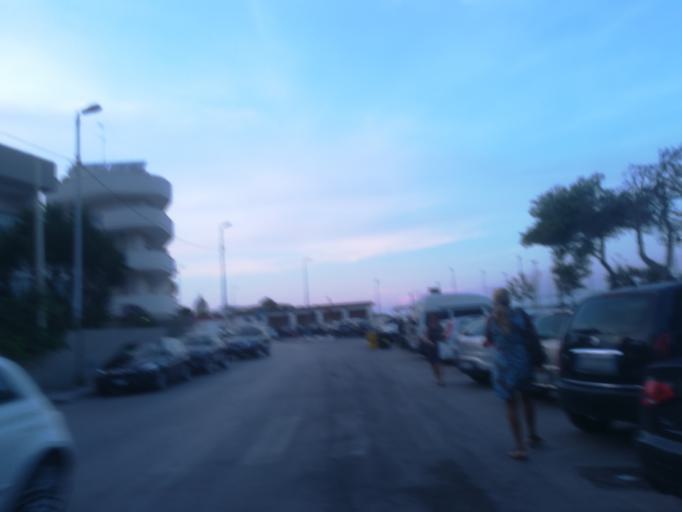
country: IT
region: Apulia
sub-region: Provincia di Bari
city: Monopoli
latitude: 40.9487
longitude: 17.3060
